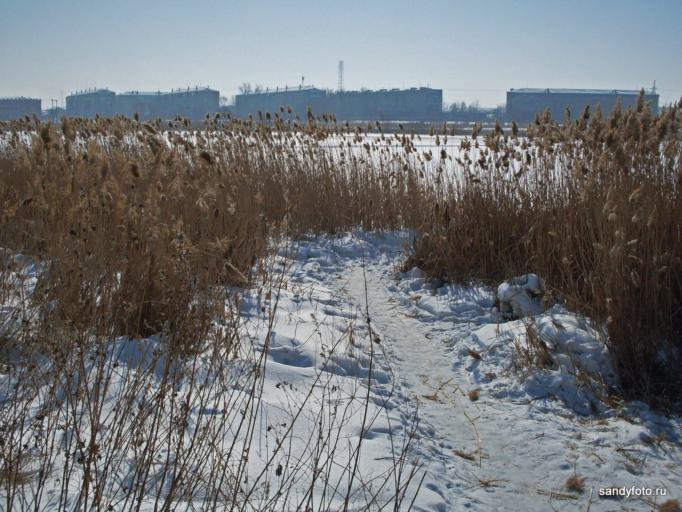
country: RU
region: Chelyabinsk
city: Troitsk
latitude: 54.0951
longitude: 61.5603
